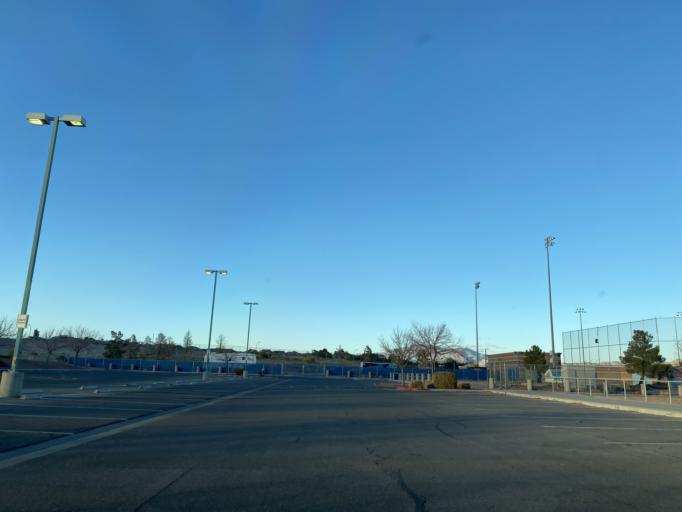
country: US
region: Nevada
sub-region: Clark County
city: Summerlin South
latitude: 36.2795
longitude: -115.3206
